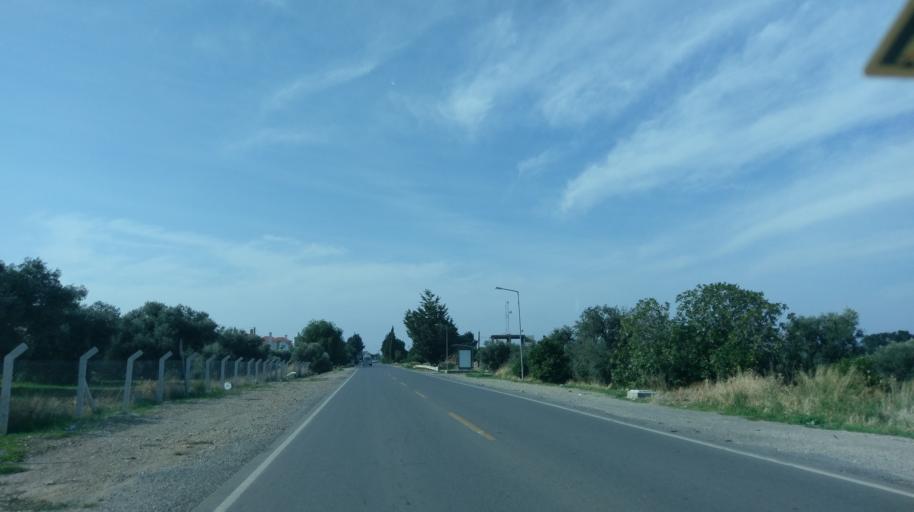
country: CY
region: Keryneia
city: Lapithos
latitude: 35.3527
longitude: 33.1241
